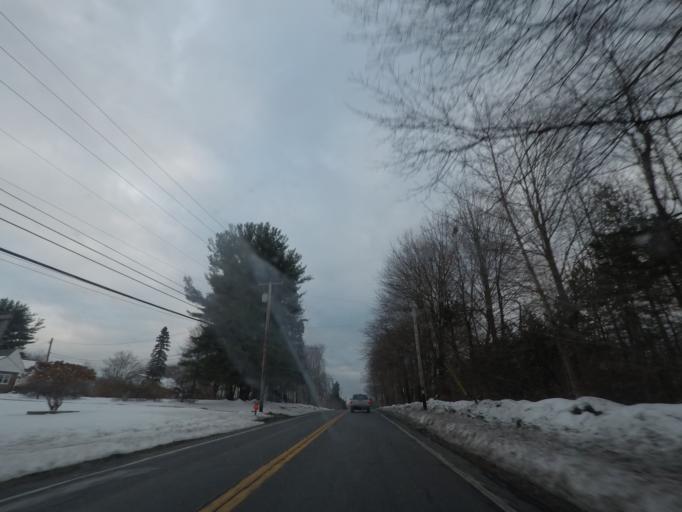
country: US
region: New York
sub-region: Ulster County
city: Plattekill
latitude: 41.6039
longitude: -74.0745
